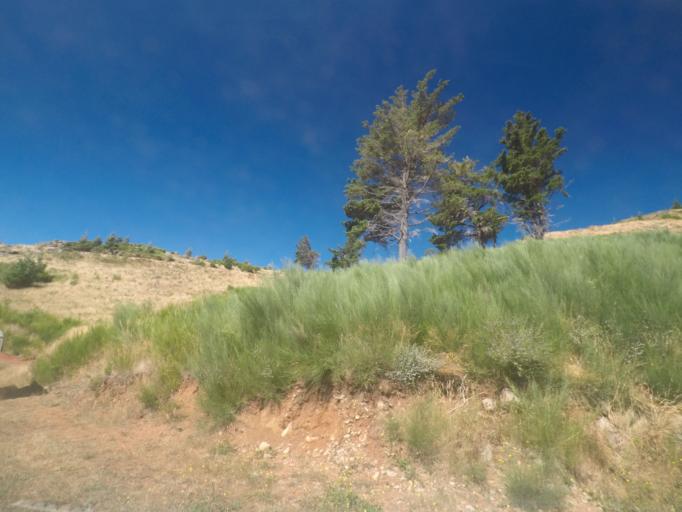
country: PT
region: Madeira
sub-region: Funchal
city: Nossa Senhora do Monte
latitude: 32.7078
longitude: -16.9065
